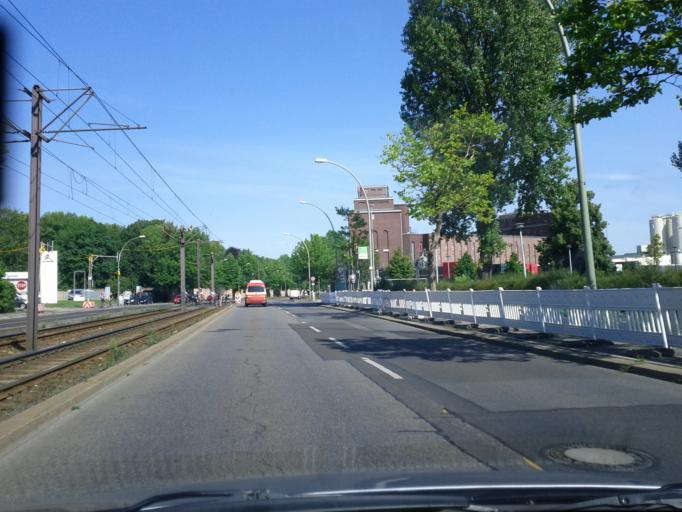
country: DE
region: Berlin
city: Fennpfuhl
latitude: 52.5394
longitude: 13.4708
